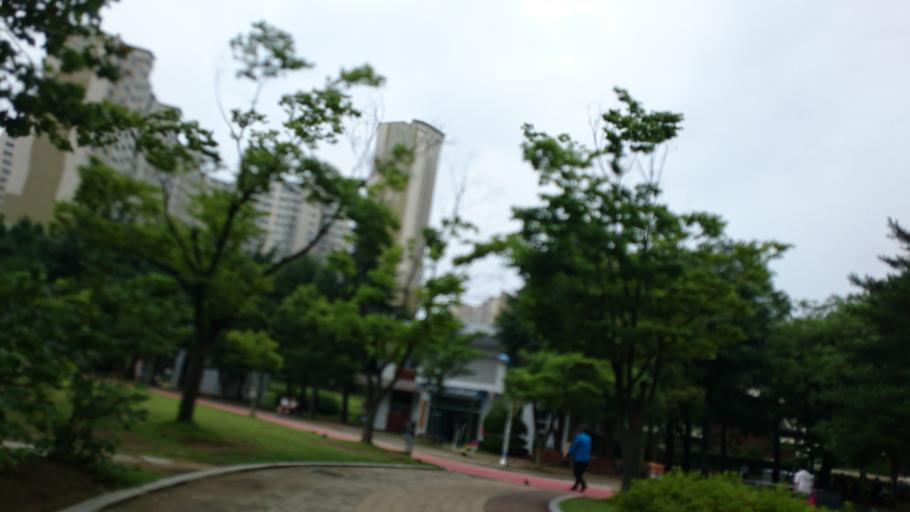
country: KR
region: Daegu
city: Daegu
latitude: 35.8713
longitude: 128.6394
